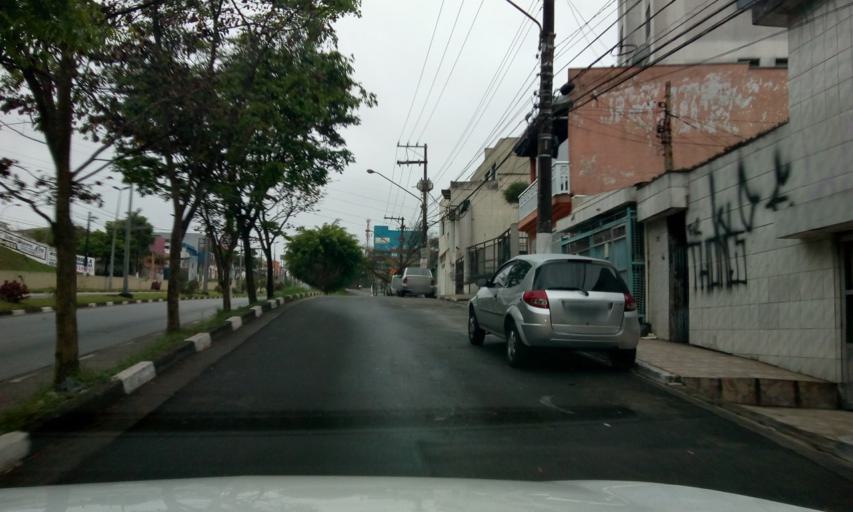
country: BR
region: Sao Paulo
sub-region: Diadema
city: Diadema
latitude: -23.6814
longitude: -46.6263
